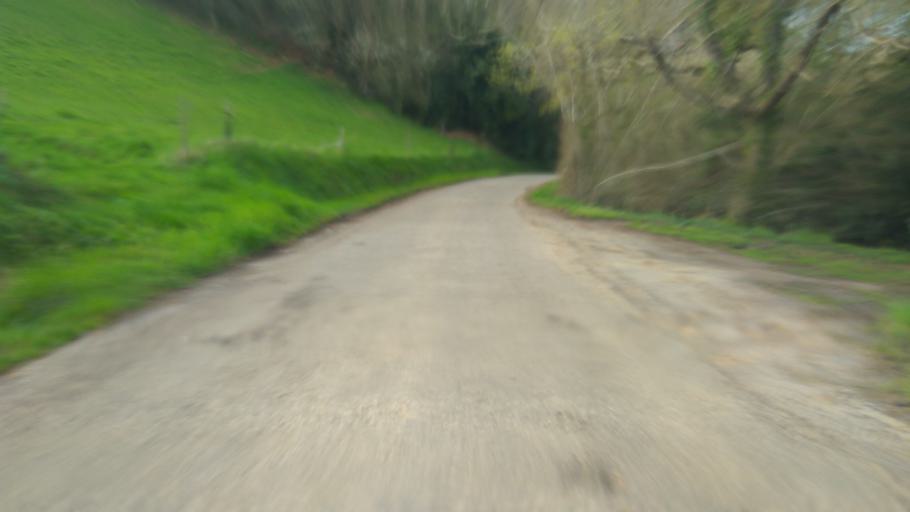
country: FR
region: Aquitaine
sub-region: Departement des Pyrenees-Atlantiques
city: Mazeres-Lezons
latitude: 43.2635
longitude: -0.3560
